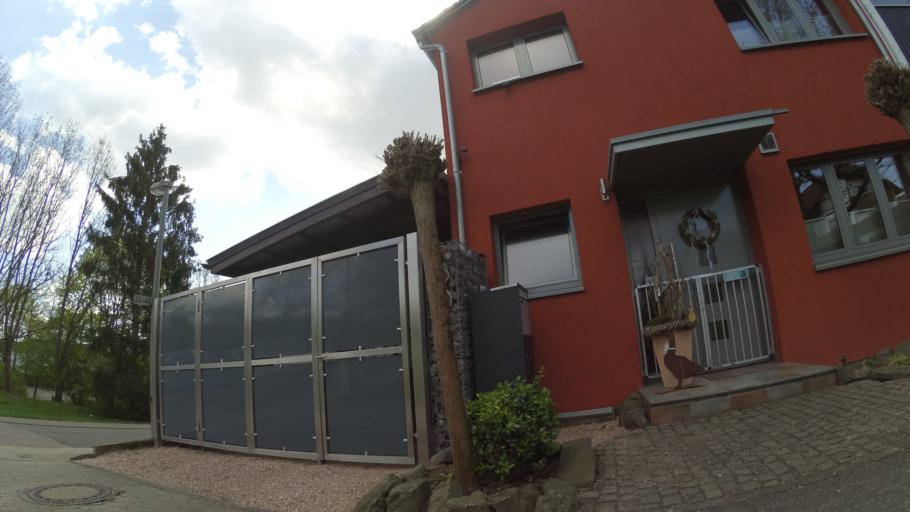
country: DE
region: Saarland
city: Riegelsberg
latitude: 49.3155
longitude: 6.9349
